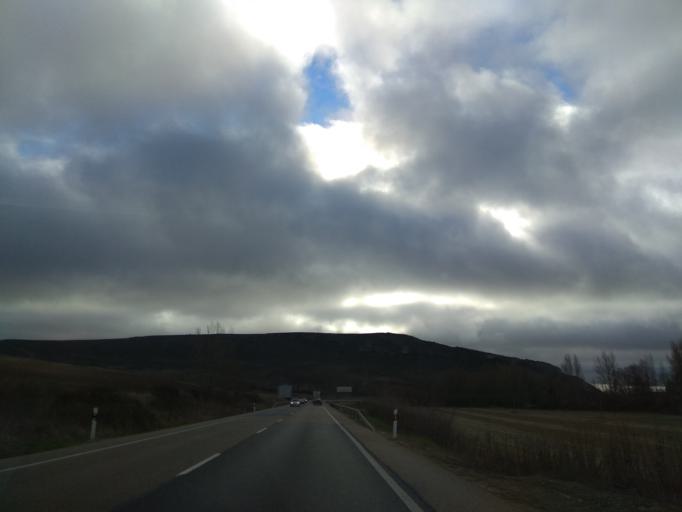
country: ES
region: Castille and Leon
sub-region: Provincia de Burgos
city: Quintanaortuno
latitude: 42.4980
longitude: -3.6975
